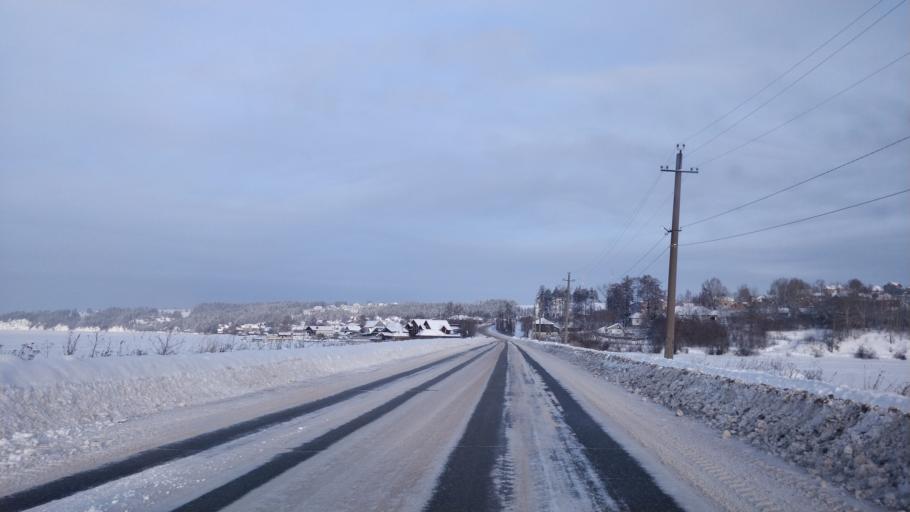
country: RU
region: Perm
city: Polazna
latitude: 58.3030
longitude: 56.4181
